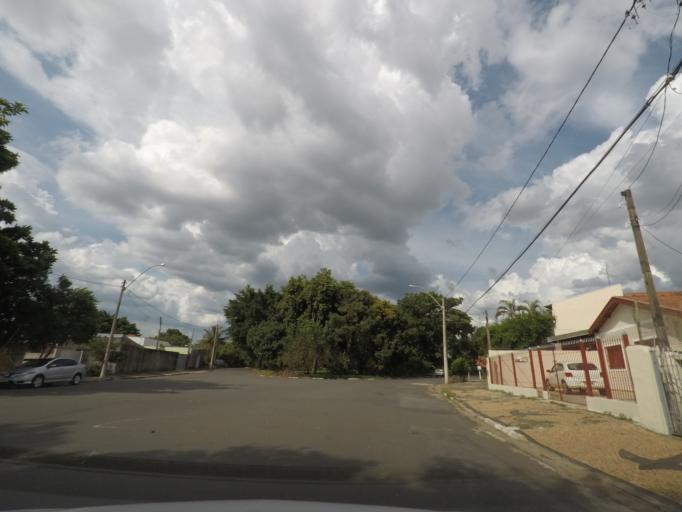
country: BR
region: Sao Paulo
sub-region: Campinas
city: Campinas
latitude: -22.8848
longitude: -47.1083
